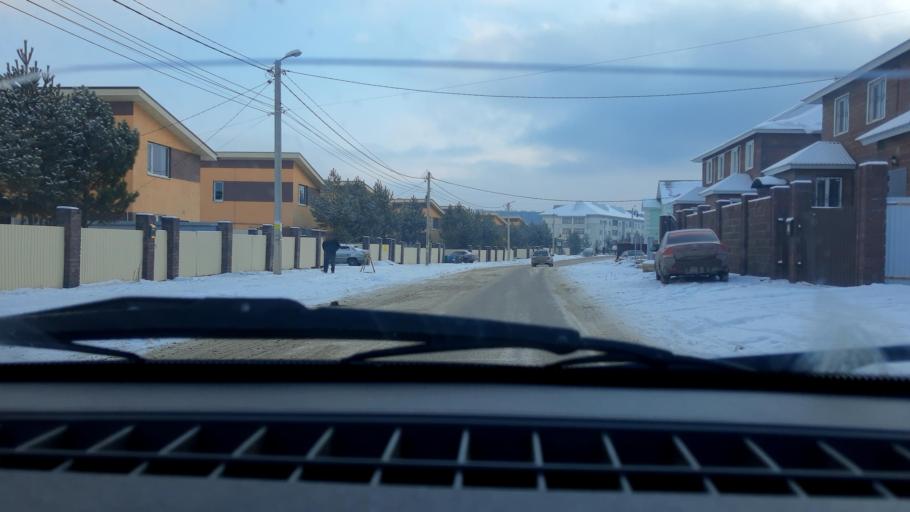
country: RU
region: Bashkortostan
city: Avdon
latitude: 54.4789
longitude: 55.8764
